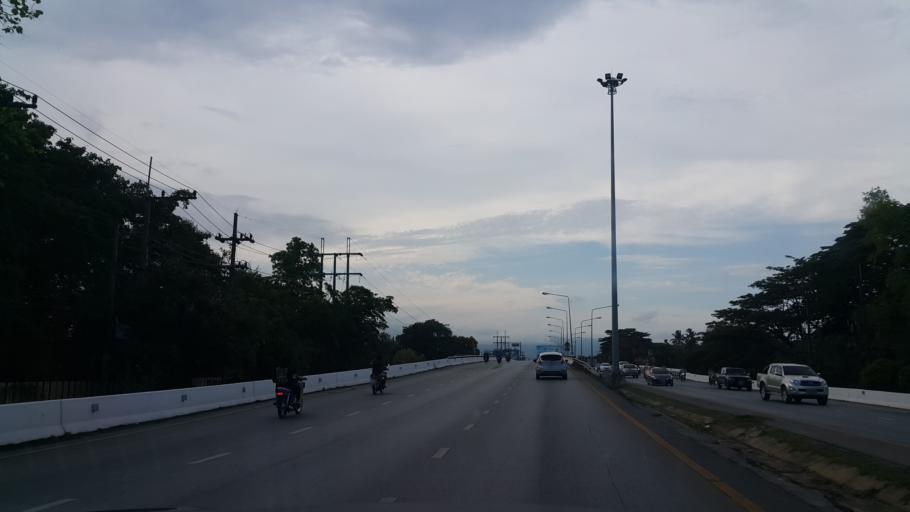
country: TH
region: Chiang Rai
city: Chiang Rai
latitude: 19.9194
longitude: 99.8466
